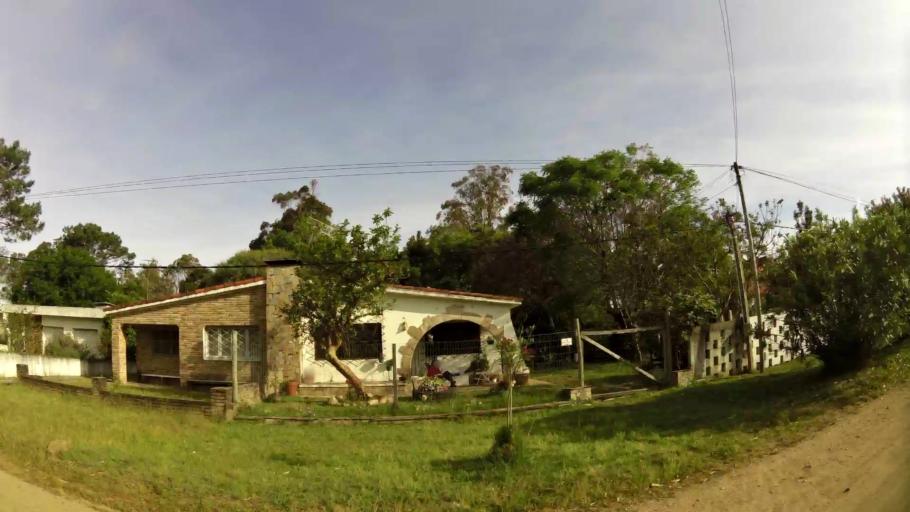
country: UY
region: Canelones
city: Atlantida
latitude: -34.7827
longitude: -55.8400
